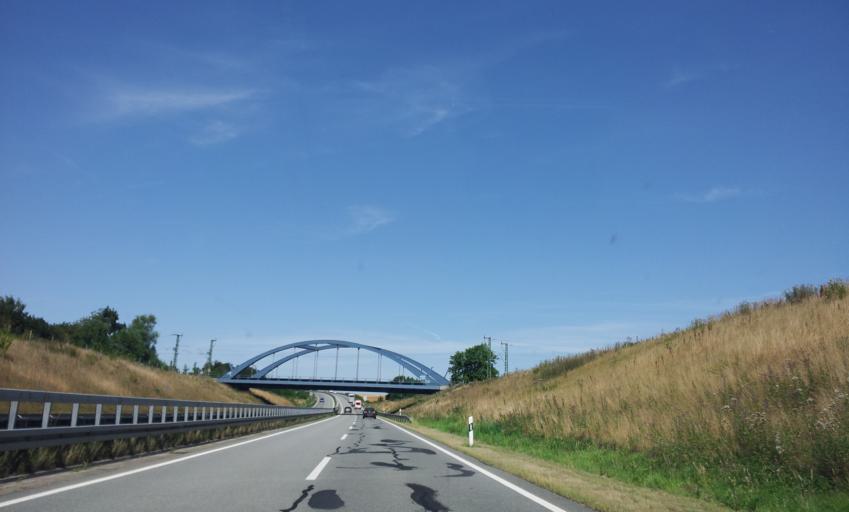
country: DE
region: Mecklenburg-Vorpommern
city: Brandshagen
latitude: 54.2195
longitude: 13.1528
